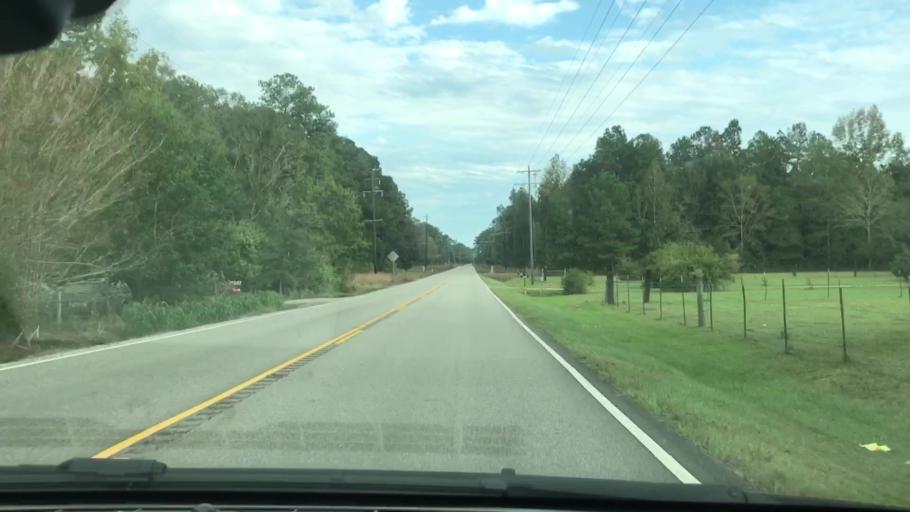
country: US
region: Louisiana
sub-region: Saint Tammany Parish
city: Abita Springs
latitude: 30.5348
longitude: -89.8979
